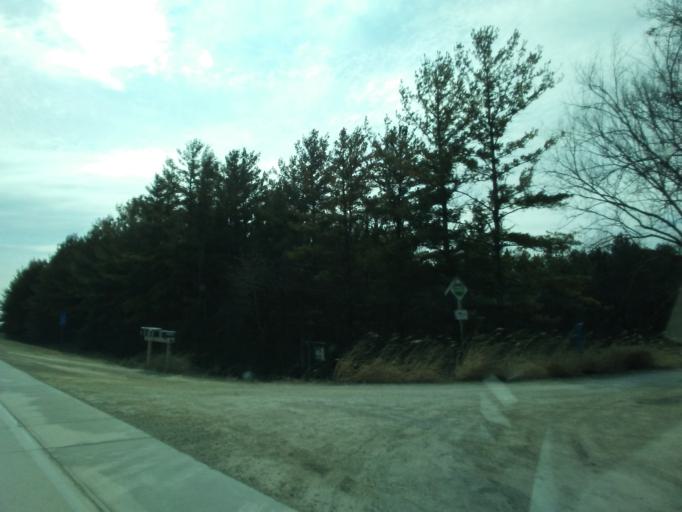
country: US
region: Iowa
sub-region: Winneshiek County
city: Decorah
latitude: 43.3368
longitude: -91.8122
